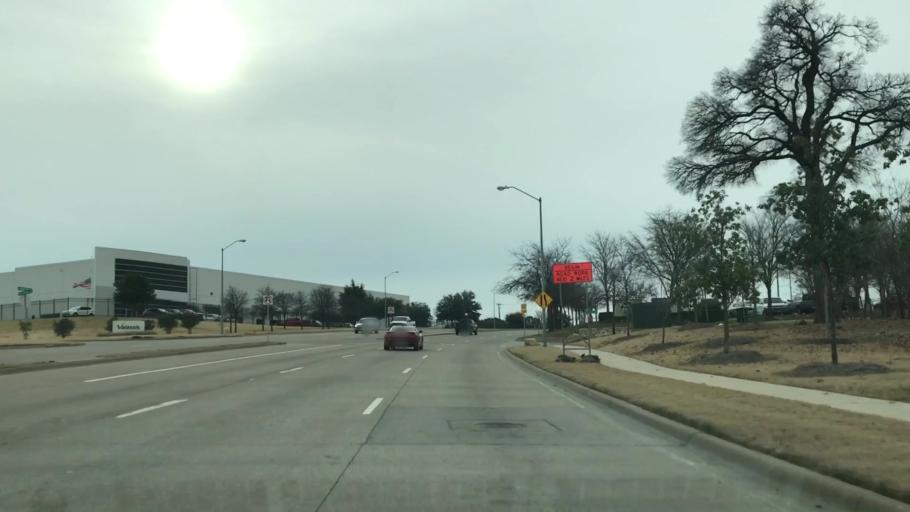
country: US
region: Texas
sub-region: Dallas County
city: Cockrell Hill
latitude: 32.7522
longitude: -96.8921
